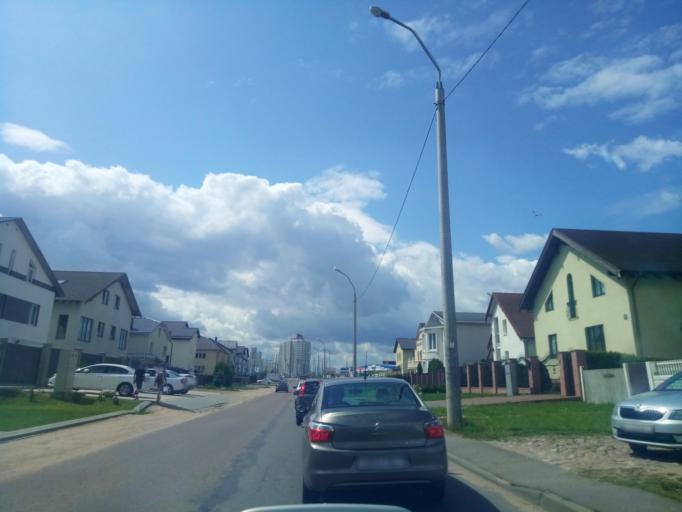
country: BY
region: Minsk
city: Zhdanovichy
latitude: 53.9376
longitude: 27.4342
